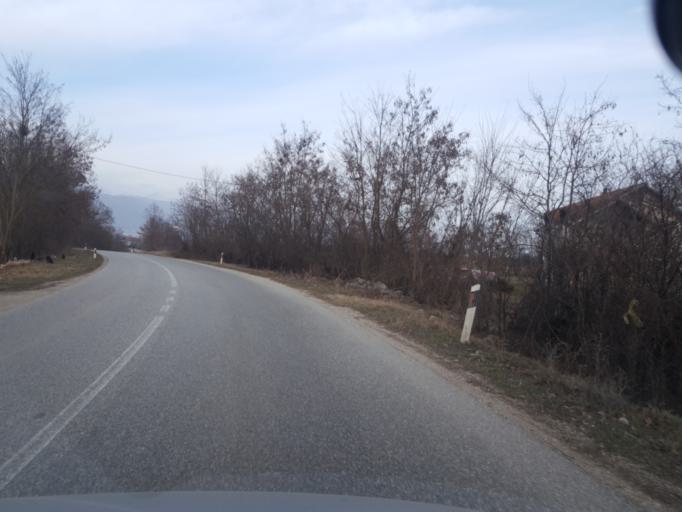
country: XK
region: Pec
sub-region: Komuna e Istogut
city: Istok
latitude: 42.7395
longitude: 20.4822
